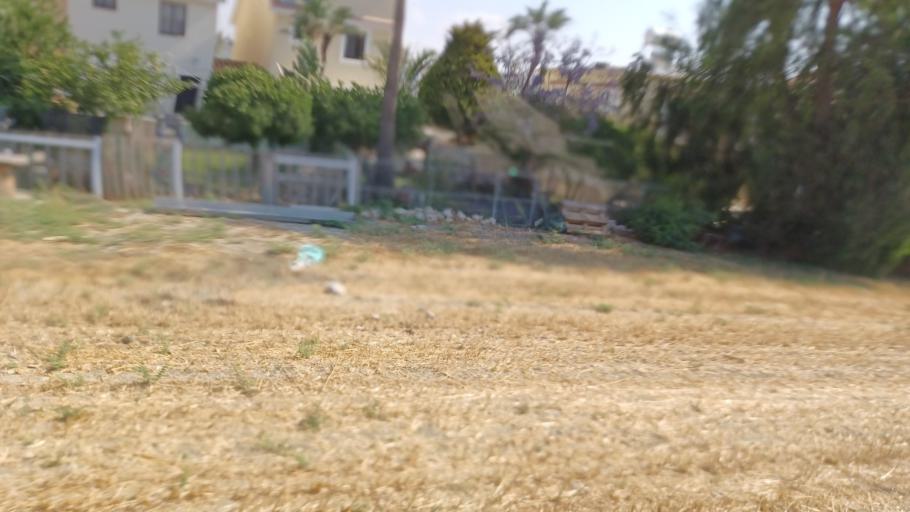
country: CY
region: Larnaka
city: Dhromolaxia
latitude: 34.9021
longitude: 33.5869
